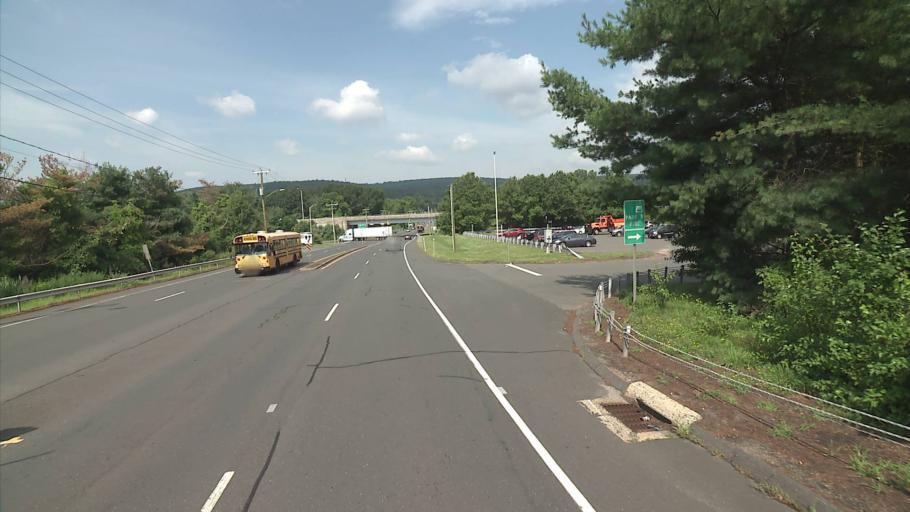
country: US
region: Connecticut
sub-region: New Haven County
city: Cheshire Village
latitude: 41.5633
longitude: -72.9151
